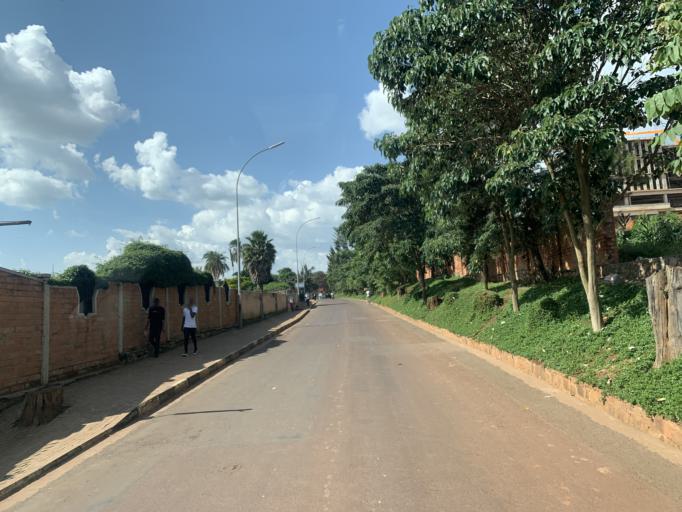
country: RW
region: Kigali
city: Kigali
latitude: -1.9598
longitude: 30.0606
